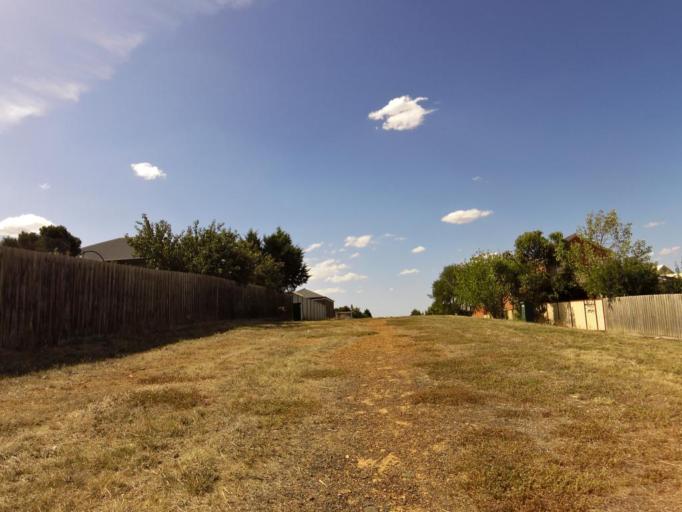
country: AU
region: Victoria
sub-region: Hume
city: Meadow Heights
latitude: -37.6598
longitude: 144.9033
